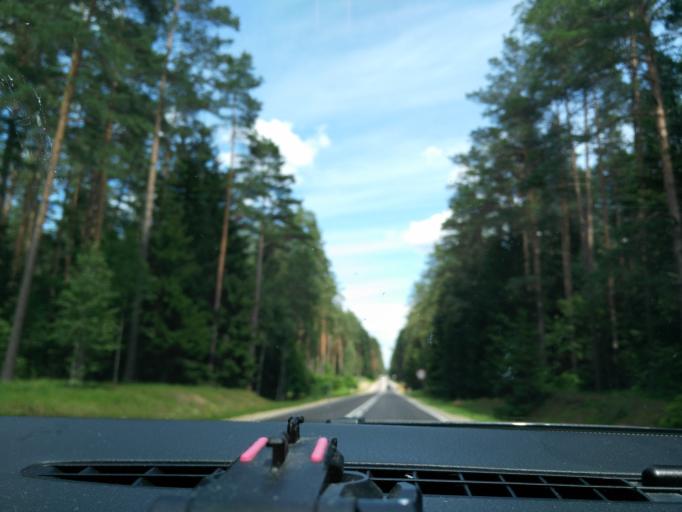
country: PL
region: Podlasie
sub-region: Powiat sejnenski
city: Krasnopol
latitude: 53.9635
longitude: 23.2356
